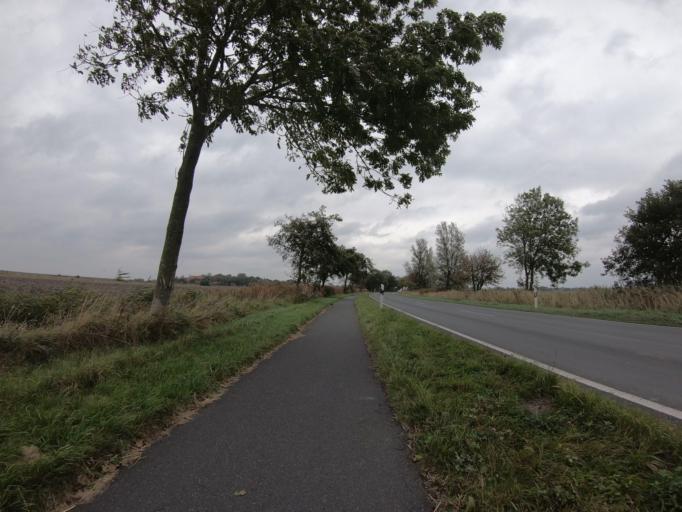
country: DE
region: Lower Saxony
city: Wirdum
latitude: 53.4924
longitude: 7.0652
